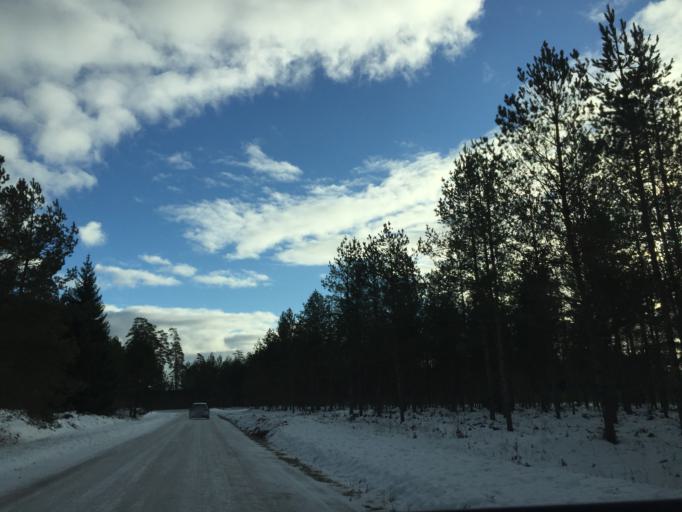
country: LV
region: Lielvarde
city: Lielvarde
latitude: 56.5638
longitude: 24.8343
